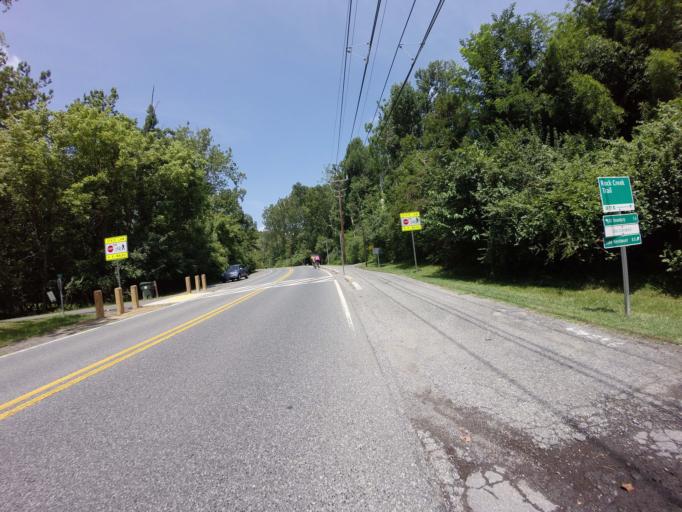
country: US
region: Maryland
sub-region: Montgomery County
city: South Kensington
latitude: 39.0195
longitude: -77.0977
